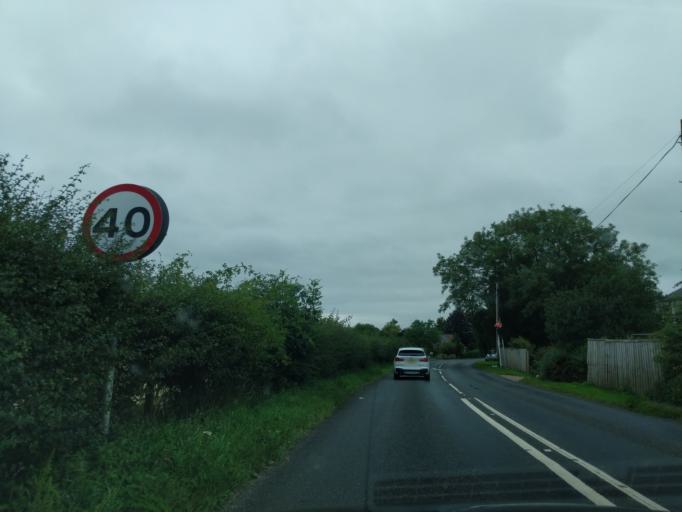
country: GB
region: Scotland
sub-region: East Lothian
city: Pencaitland
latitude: 55.9086
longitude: -2.9110
